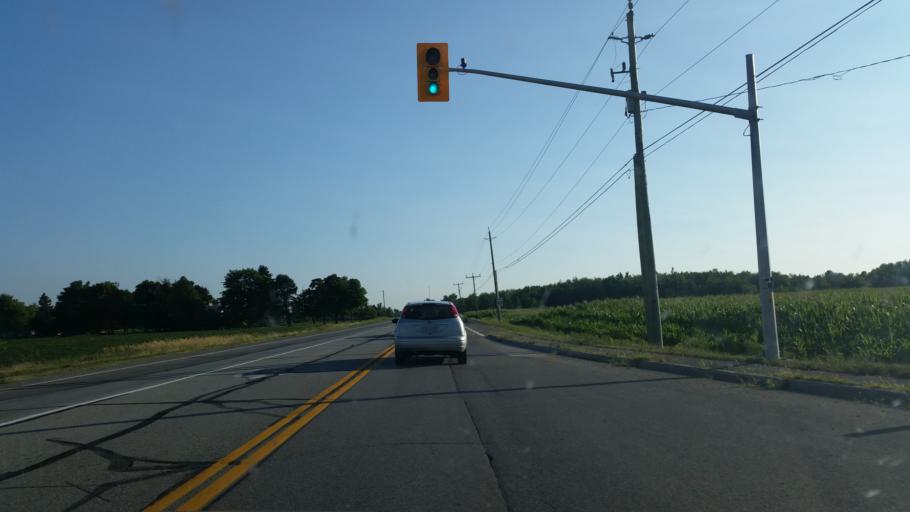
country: CA
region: Ontario
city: Brampton
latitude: 43.8119
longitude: -79.8359
